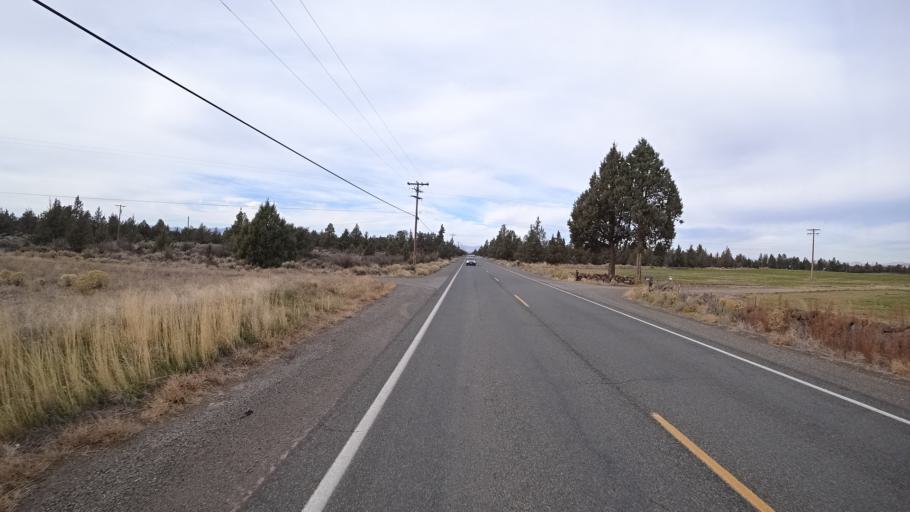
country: US
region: California
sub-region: Siskiyou County
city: Weed
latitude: 41.5989
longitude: -122.3449
